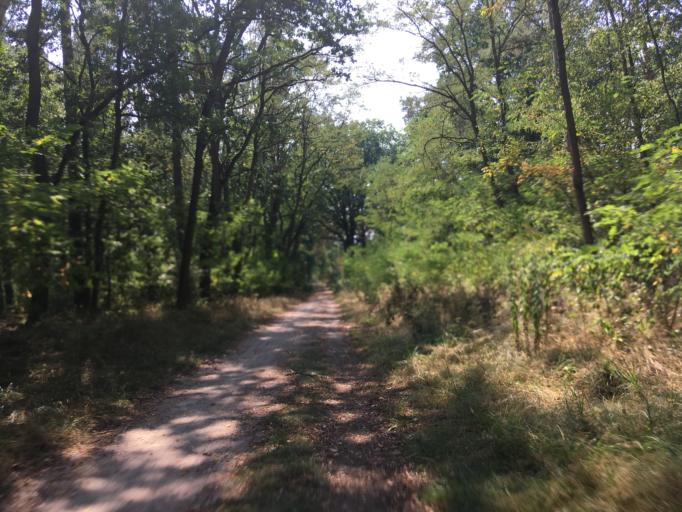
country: DE
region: Berlin
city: Friedrichshagen
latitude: 52.4599
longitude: 13.6038
